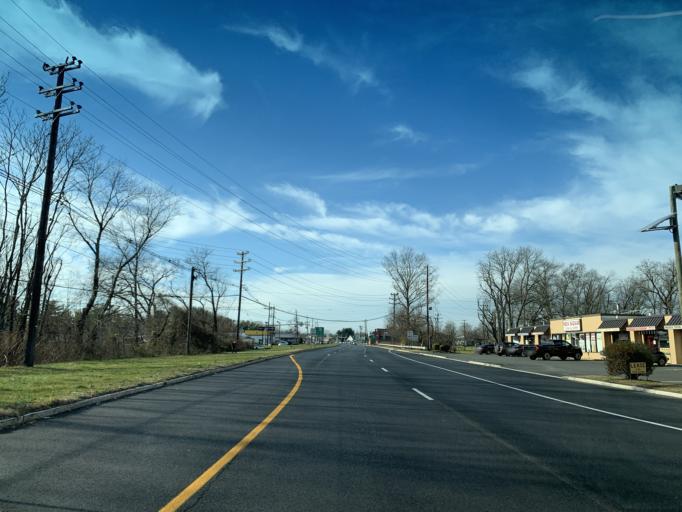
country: US
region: New Jersey
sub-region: Burlington County
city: Burlington
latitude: 40.0713
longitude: -74.8588
